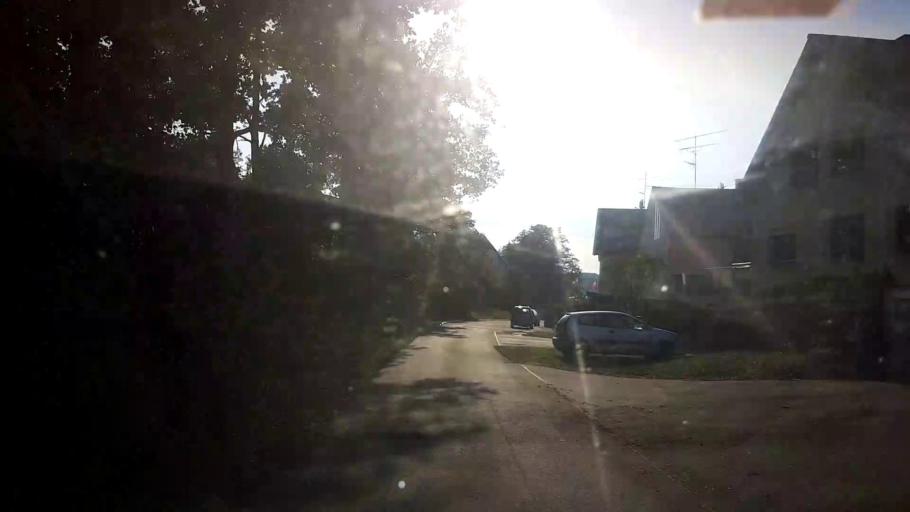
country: DE
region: Bavaria
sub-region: Upper Franconia
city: Stegaurach
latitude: 49.8727
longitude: 10.8175
